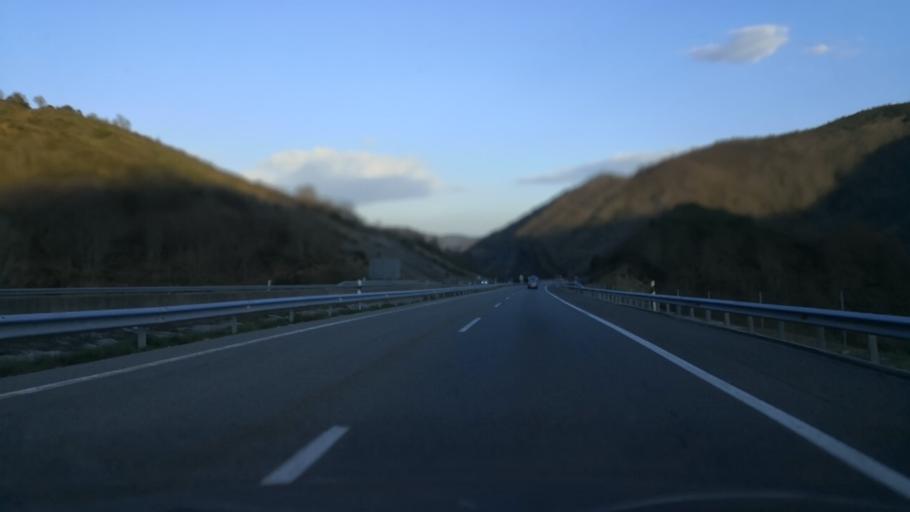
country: ES
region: Castille and Leon
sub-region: Provincia de Leon
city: Vega de Valcarce
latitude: 42.6679
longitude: -6.9457
